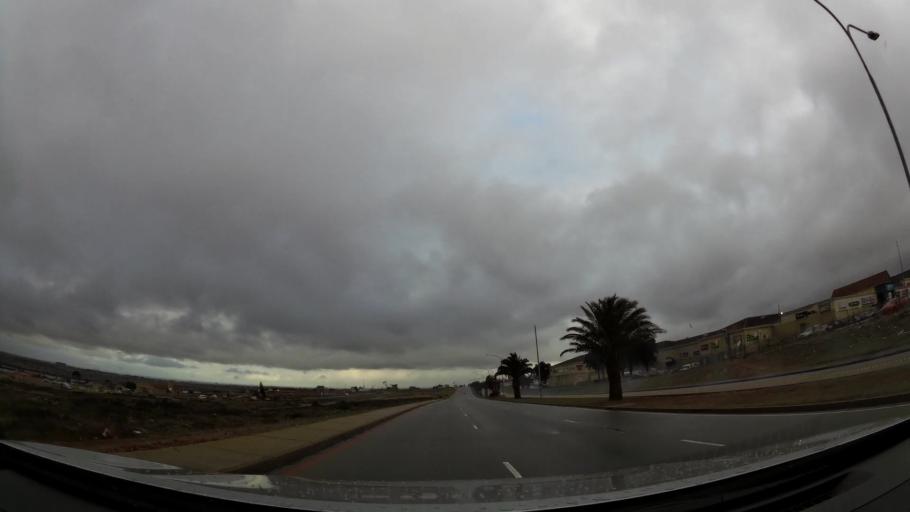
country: ZA
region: Eastern Cape
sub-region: Nelson Mandela Bay Metropolitan Municipality
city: Port Elizabeth
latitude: -33.8928
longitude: 25.5267
